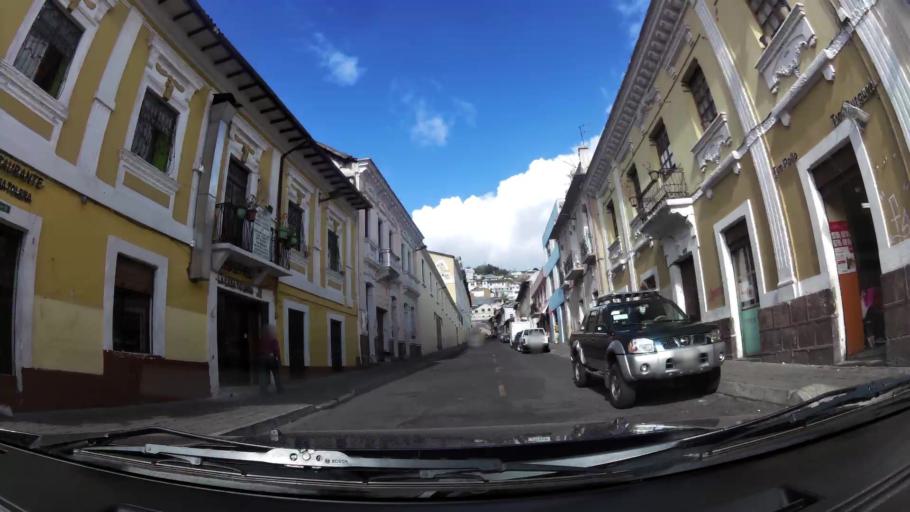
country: EC
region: Pichincha
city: Quito
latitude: -0.2231
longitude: -78.5059
